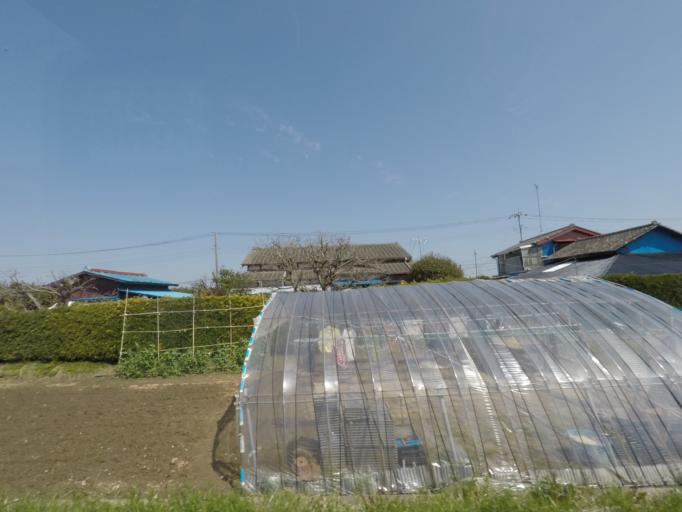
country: JP
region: Ibaraki
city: Edosaki
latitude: 35.8691
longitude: 140.2993
